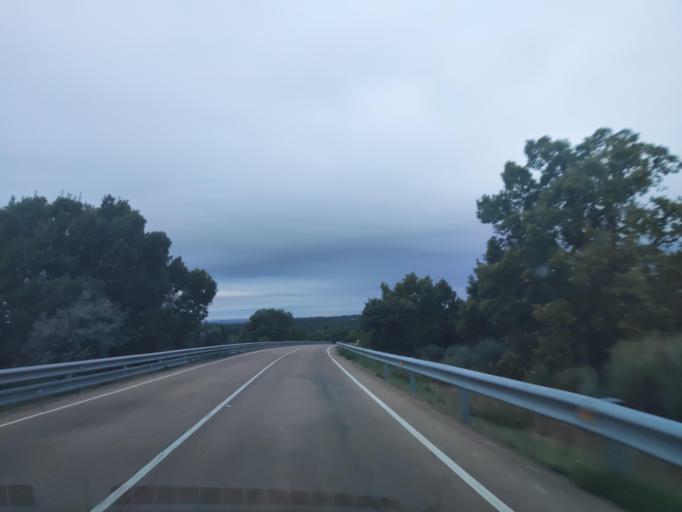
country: ES
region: Castille and Leon
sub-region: Provincia de Salamanca
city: Sobradillo
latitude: 40.9489
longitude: -6.7753
